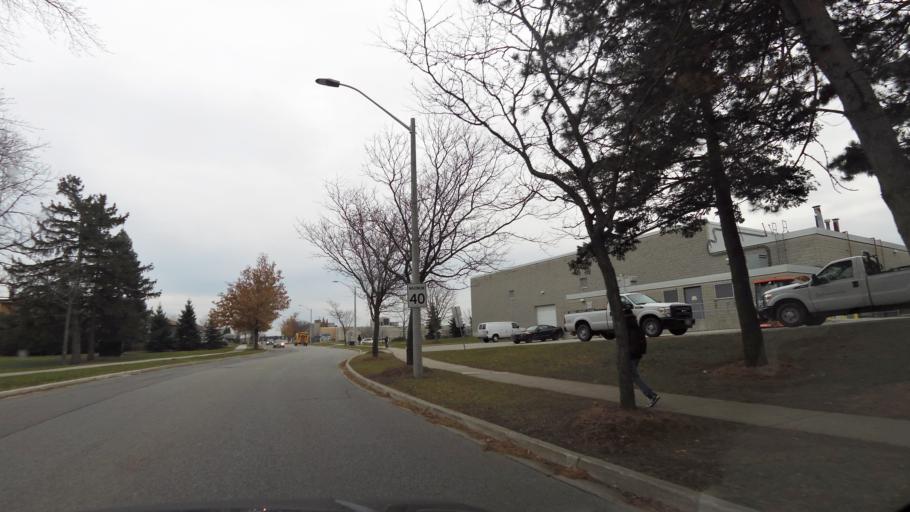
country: CA
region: Ontario
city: Etobicoke
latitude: 43.6237
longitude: -79.5980
